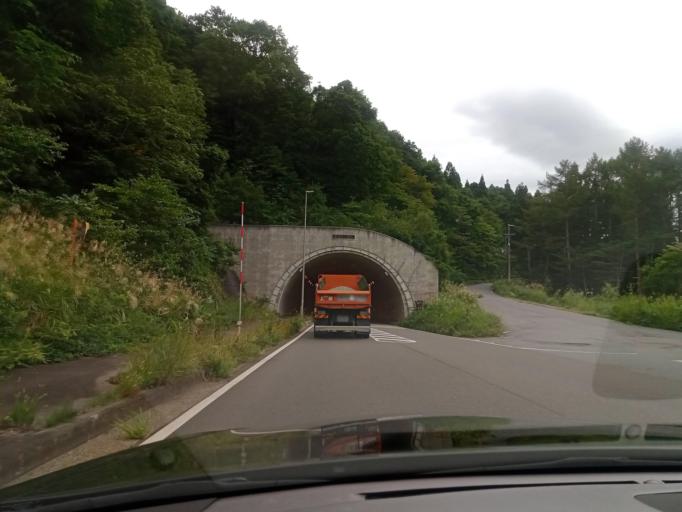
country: JP
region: Niigata
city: Arai
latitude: 36.8405
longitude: 138.2035
